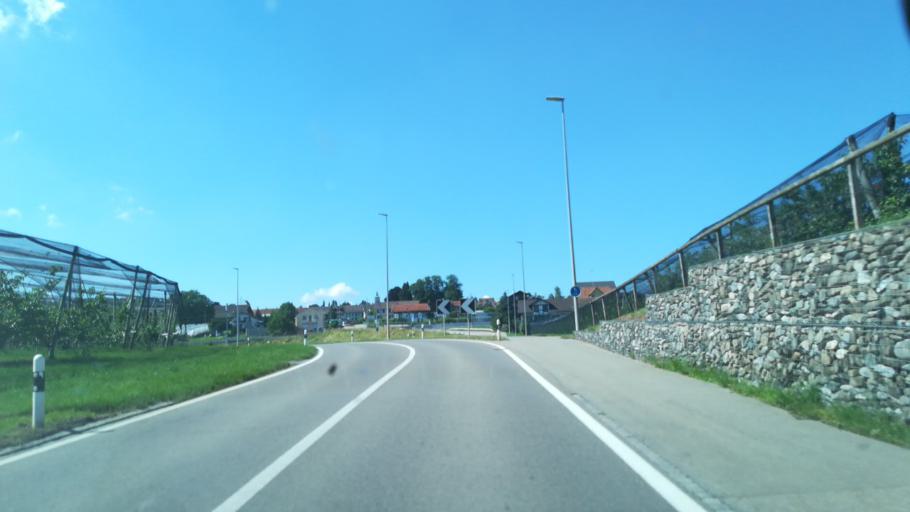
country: CH
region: Thurgau
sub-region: Weinfelden District
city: Berg
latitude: 47.5702
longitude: 9.1699
